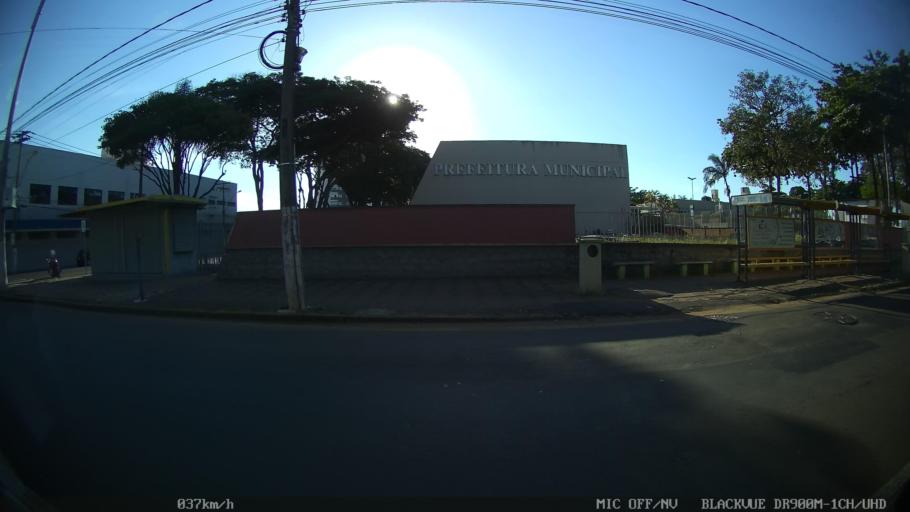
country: BR
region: Sao Paulo
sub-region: Franca
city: Franca
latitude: -20.5287
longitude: -47.3929
